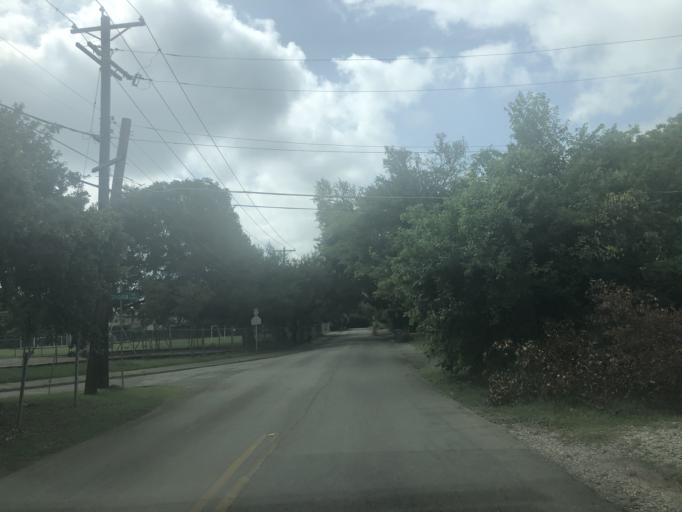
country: US
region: Texas
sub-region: Dallas County
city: University Park
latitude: 32.8549
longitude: -96.8326
